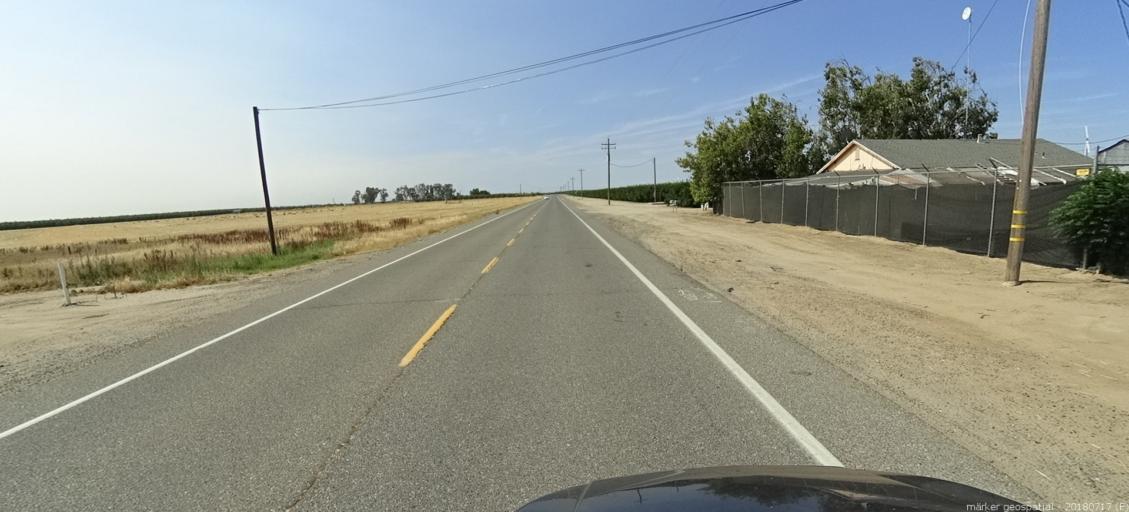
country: US
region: California
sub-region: Madera County
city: Fairmead
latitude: 37.0620
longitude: -120.1471
